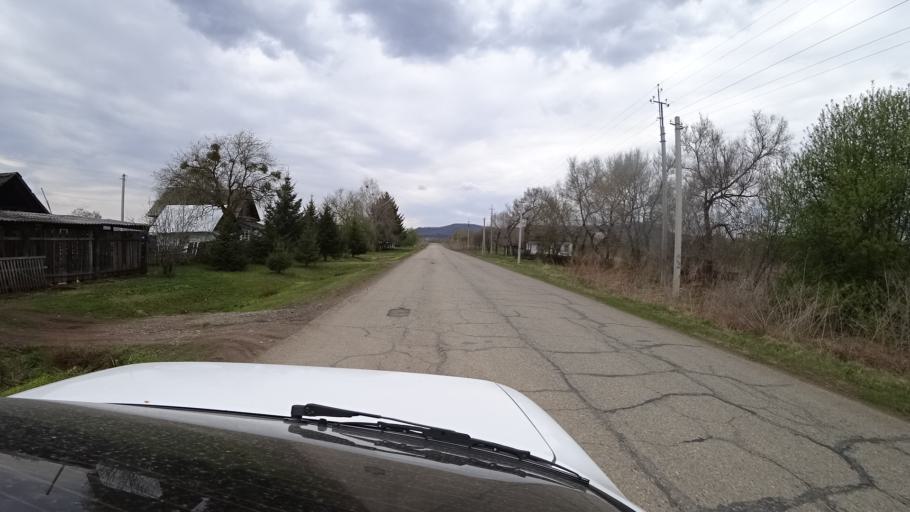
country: RU
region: Primorskiy
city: Novopokrovka
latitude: 45.5521
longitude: 134.3615
